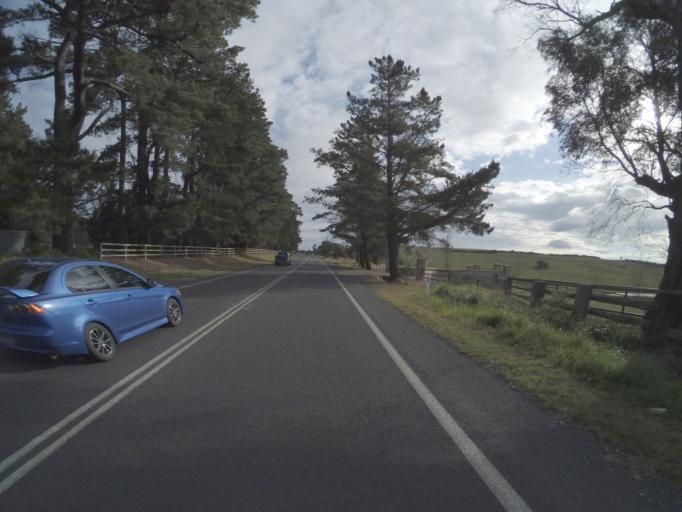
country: AU
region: New South Wales
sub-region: Wingecarribee
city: Moss Vale
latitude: -34.5814
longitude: 150.3002
